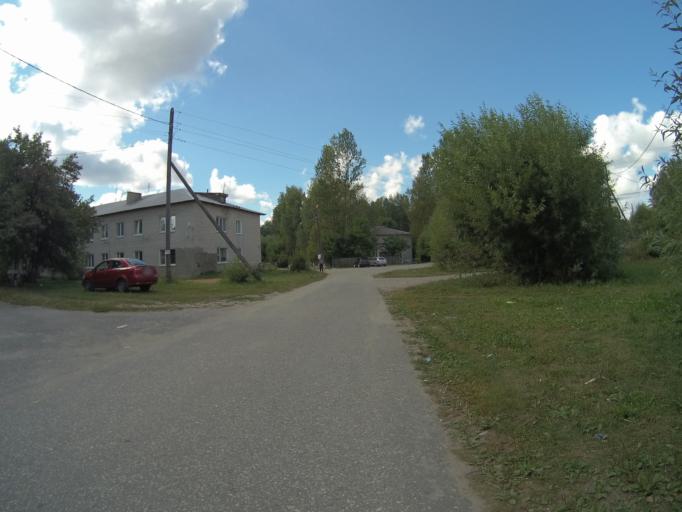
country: RU
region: Vladimir
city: Golovino
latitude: 55.9139
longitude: 40.6050
